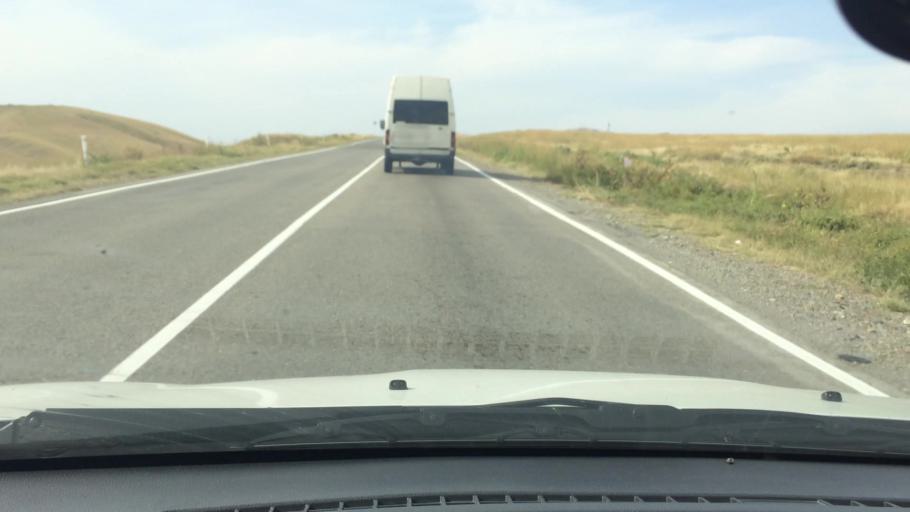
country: GE
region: Kvemo Kartli
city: Rust'avi
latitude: 41.5228
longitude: 44.9848
